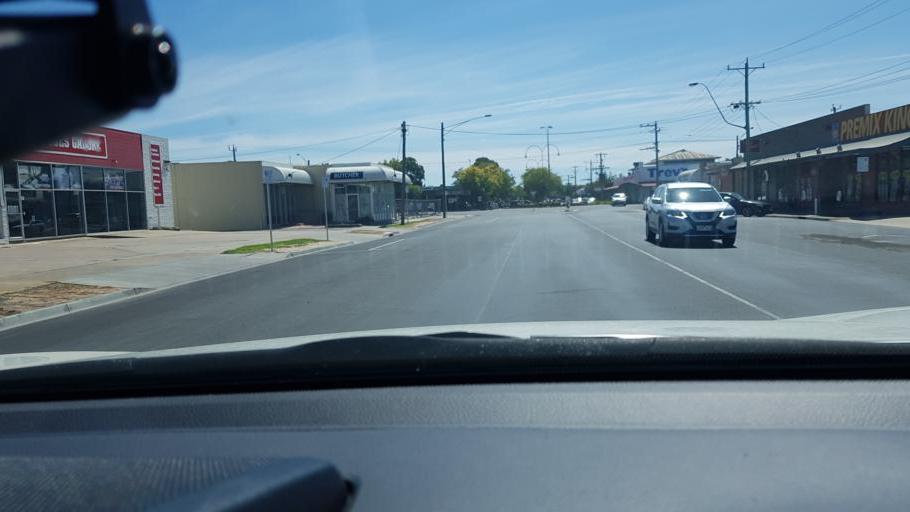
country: AU
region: Victoria
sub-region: Horsham
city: Horsham
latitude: -36.7177
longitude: 142.1971
